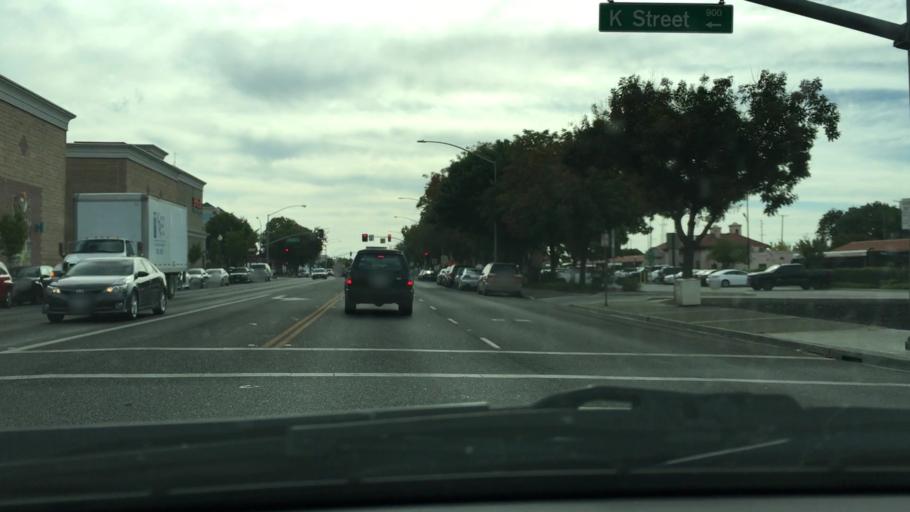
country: US
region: California
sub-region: Stanislaus County
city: Modesto
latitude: 37.6407
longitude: -121.0025
